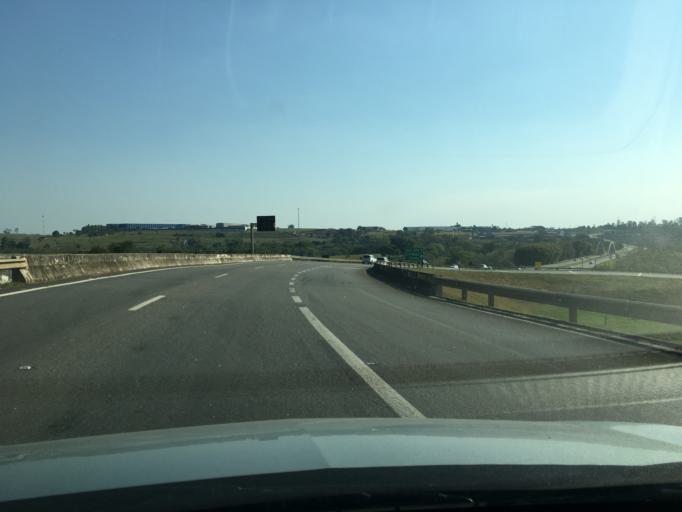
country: BR
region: Sao Paulo
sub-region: Sao Joao Da Boa Vista
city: Sao Joao da Boa Vista
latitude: -21.9912
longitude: -46.7924
